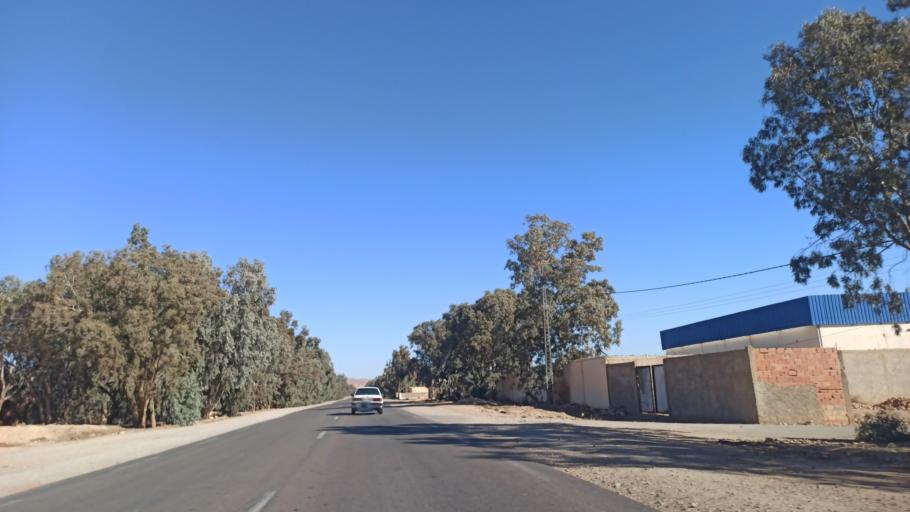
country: TN
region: Gafsa
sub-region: Gafsa Municipality
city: Gafsa
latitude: 34.3920
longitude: 8.7132
